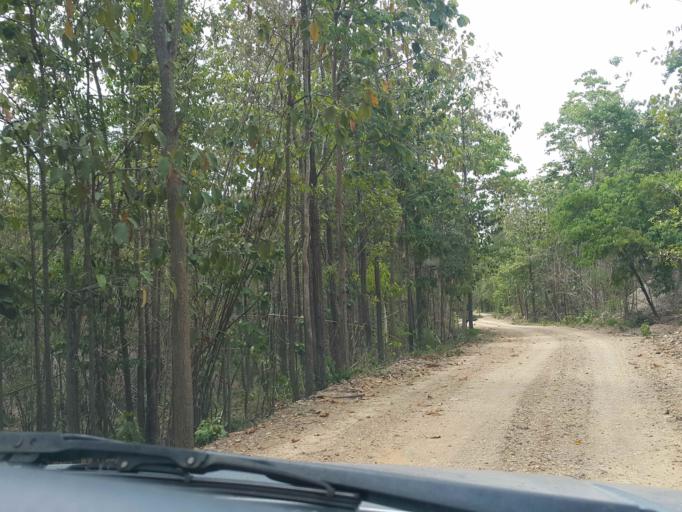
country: TH
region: Chiang Mai
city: Doi Lo
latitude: 18.5208
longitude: 98.7441
